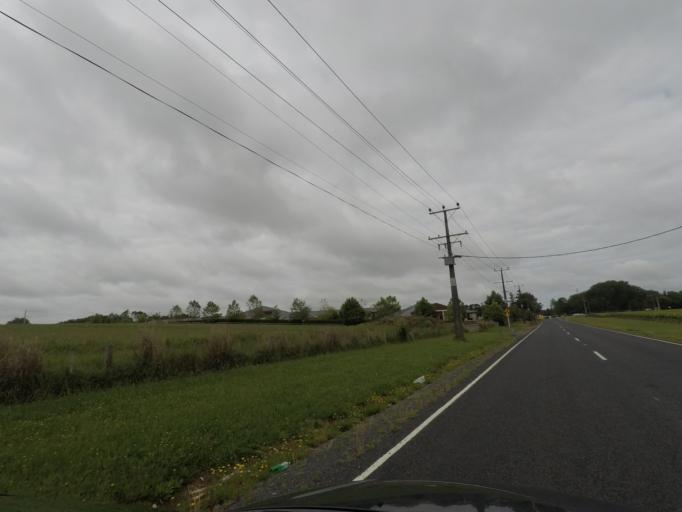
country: NZ
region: Auckland
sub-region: Auckland
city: Muriwai Beach
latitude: -36.7779
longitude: 174.5695
